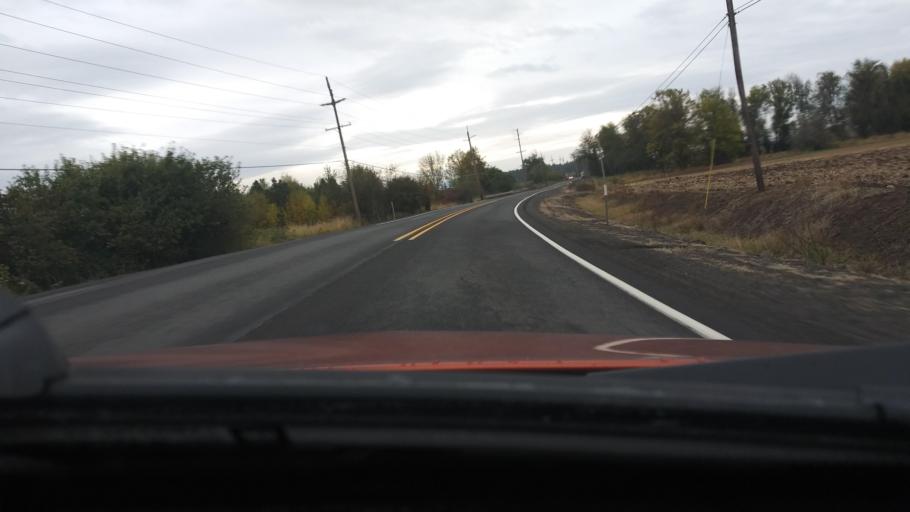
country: US
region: Oregon
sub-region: Washington County
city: Banks
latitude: 45.5752
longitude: -123.1095
